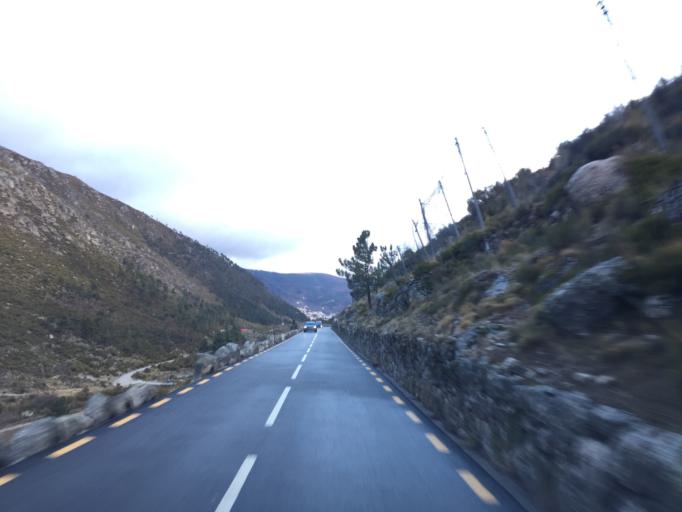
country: PT
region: Guarda
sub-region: Manteigas
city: Manteigas
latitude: 40.3533
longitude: -7.5590
